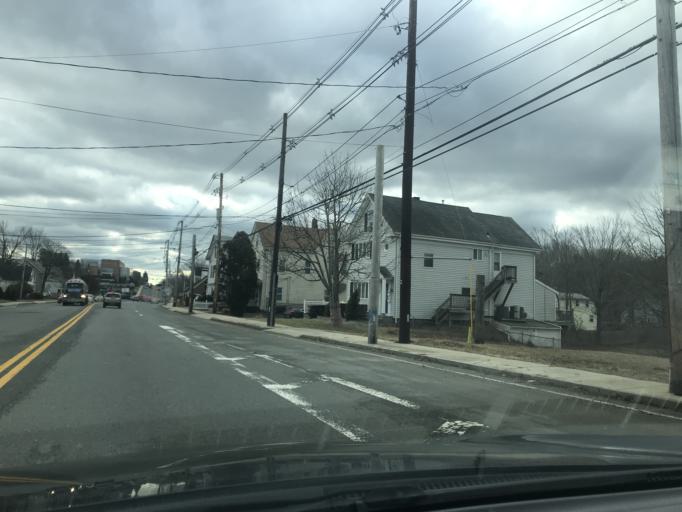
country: US
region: Massachusetts
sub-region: Norfolk County
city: Weymouth
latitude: 42.1820
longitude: -70.9553
